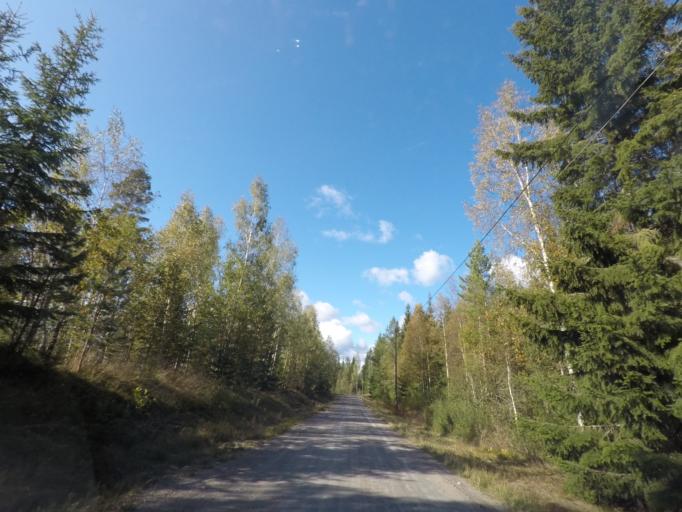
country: SE
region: Vaestmanland
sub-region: Skinnskattebergs Kommun
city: Skinnskatteberg
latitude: 59.8264
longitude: 15.5173
